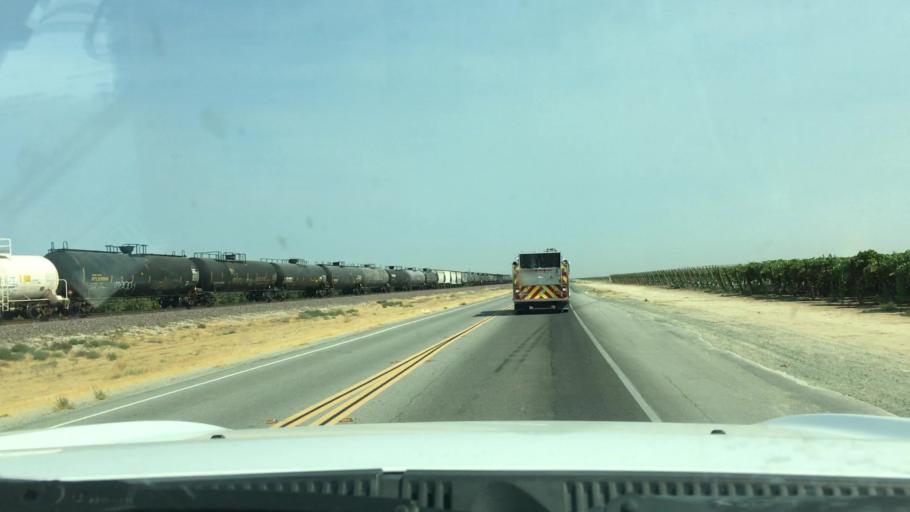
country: US
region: California
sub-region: Kern County
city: Delano
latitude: 35.7787
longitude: -119.3514
